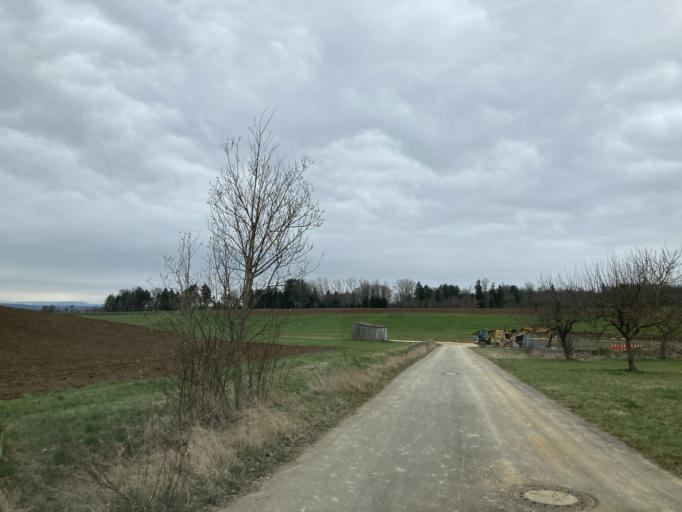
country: DE
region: Baden-Wuerttemberg
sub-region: Regierungsbezirk Stuttgart
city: Bondorf
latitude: 48.5080
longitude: 8.8548
